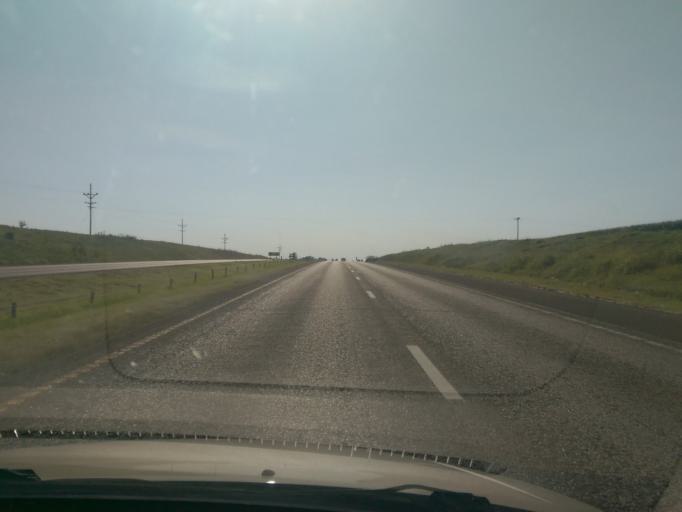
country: US
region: Missouri
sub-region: Lafayette County
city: Concordia
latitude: 38.9878
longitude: -93.5161
